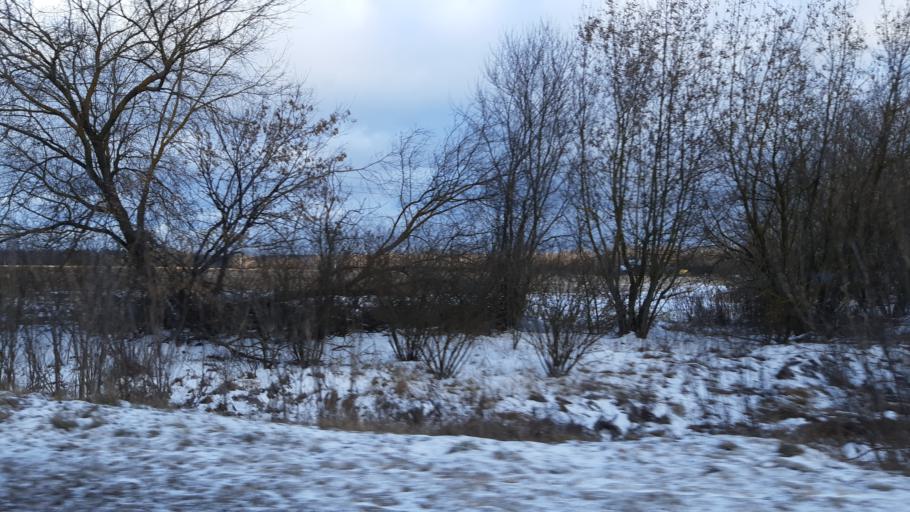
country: RU
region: Moskovskaya
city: Noginsk-9
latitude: 56.0229
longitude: 38.5564
